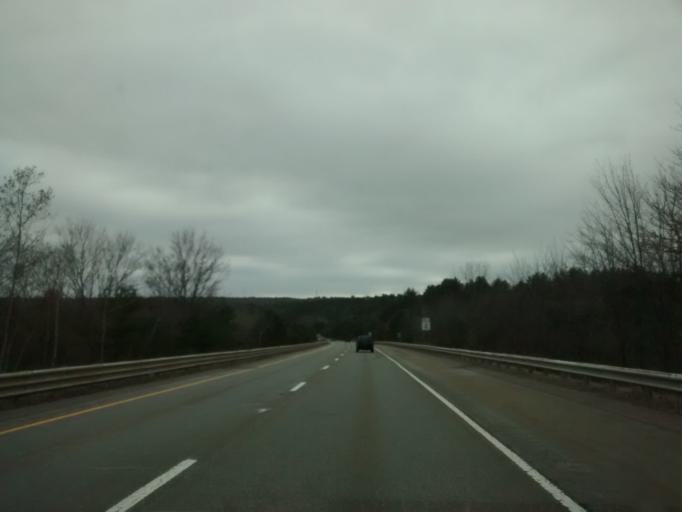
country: US
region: Massachusetts
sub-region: Worcester County
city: Templeton
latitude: 42.5710
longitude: -72.0819
